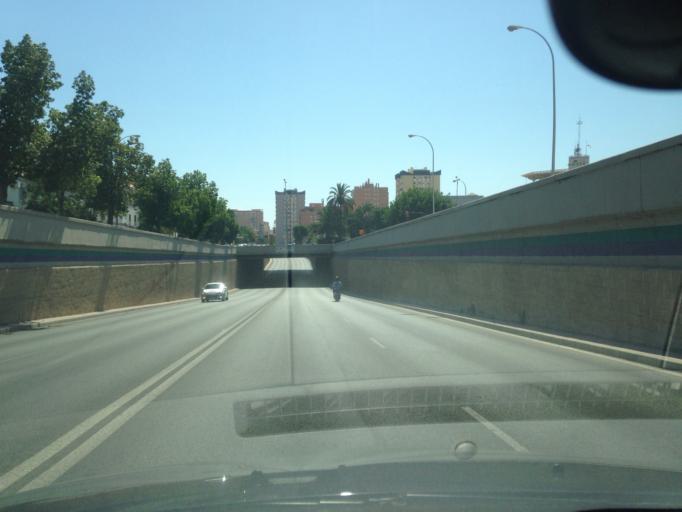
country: ES
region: Andalusia
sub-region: Provincia de Malaga
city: Malaga
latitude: 36.7163
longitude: -4.4484
